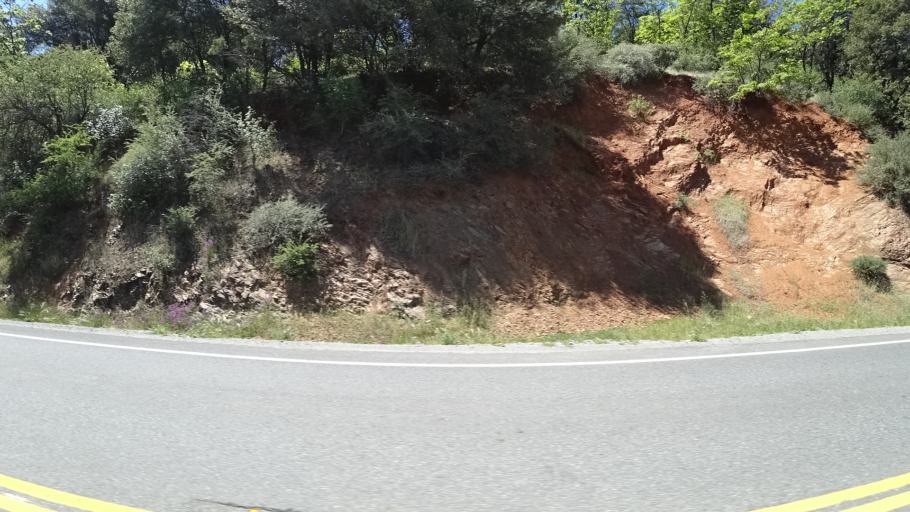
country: US
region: California
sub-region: Trinity County
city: Weaverville
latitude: 40.7348
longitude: -123.0164
